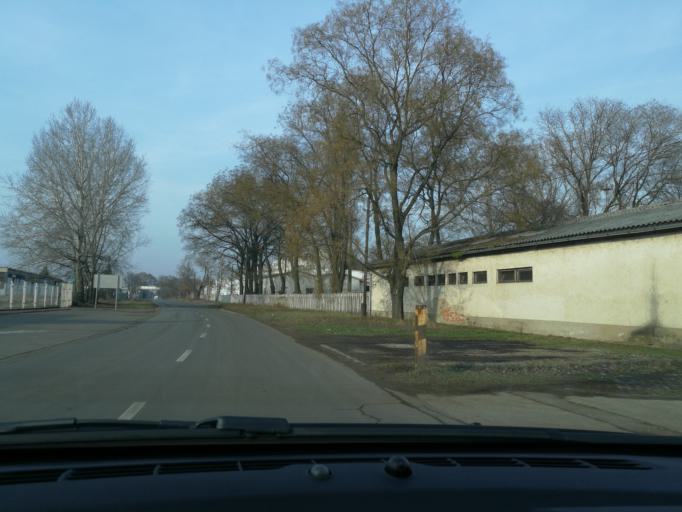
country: HU
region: Szabolcs-Szatmar-Bereg
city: Nyiregyhaza
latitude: 47.9463
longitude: 21.7025
